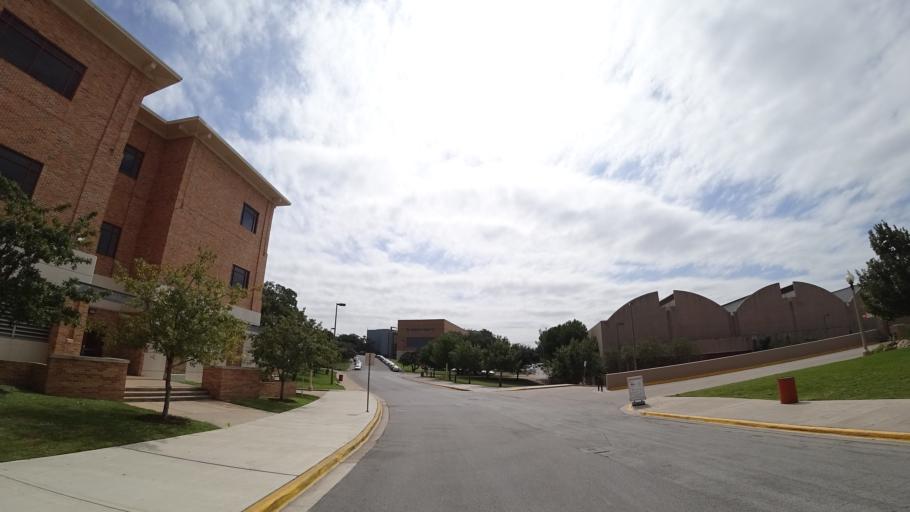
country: US
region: Texas
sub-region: Travis County
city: Austin
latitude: 30.2821
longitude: -97.7315
